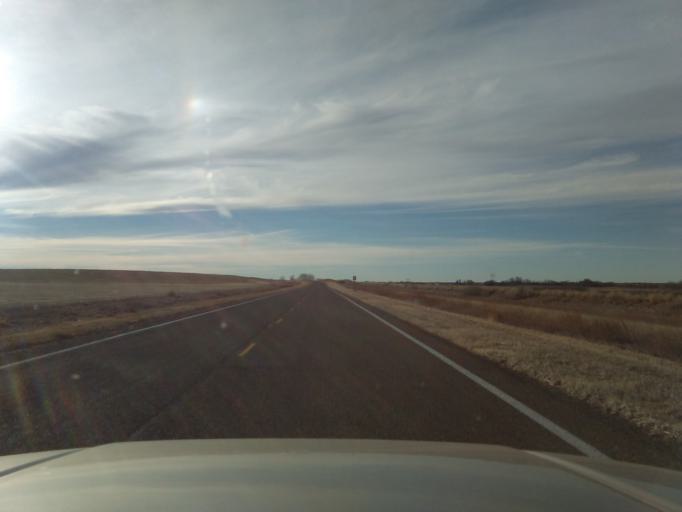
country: US
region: Kansas
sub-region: Norton County
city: Norton
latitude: 39.7528
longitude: -100.1351
